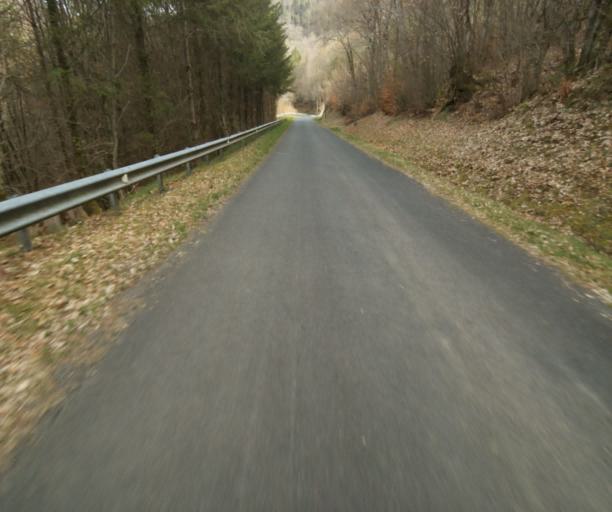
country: FR
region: Limousin
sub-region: Departement de la Correze
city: Correze
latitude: 45.4255
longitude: 1.8015
